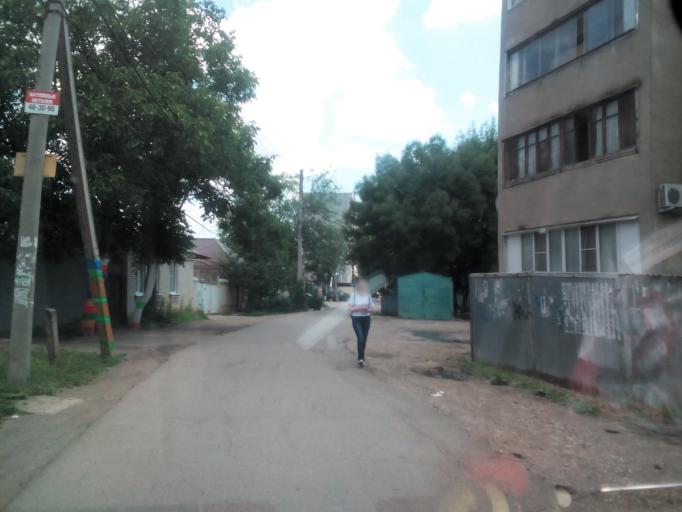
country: RU
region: Stavropol'skiy
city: Pyatigorsk
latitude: 44.0502
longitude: 43.0445
